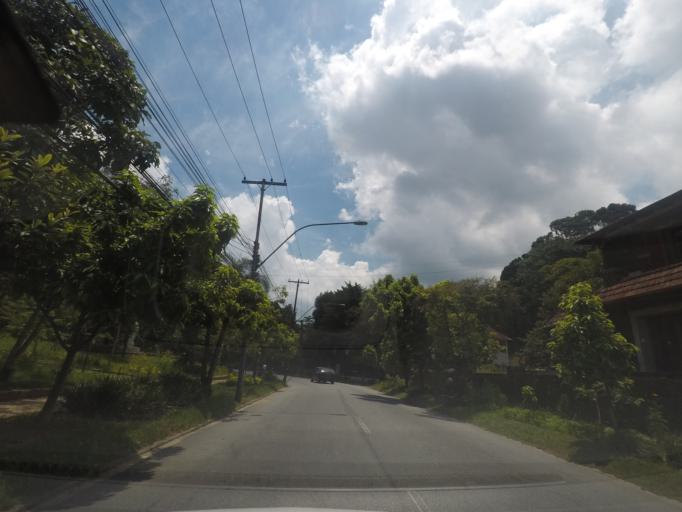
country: BR
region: Rio de Janeiro
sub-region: Petropolis
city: Petropolis
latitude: -22.5051
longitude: -43.1791
